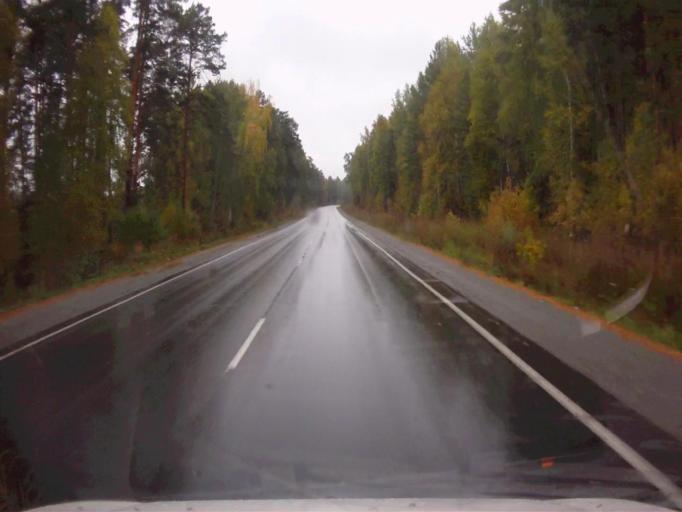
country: RU
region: Chelyabinsk
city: Kyshtym
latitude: 55.6392
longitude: 60.5923
